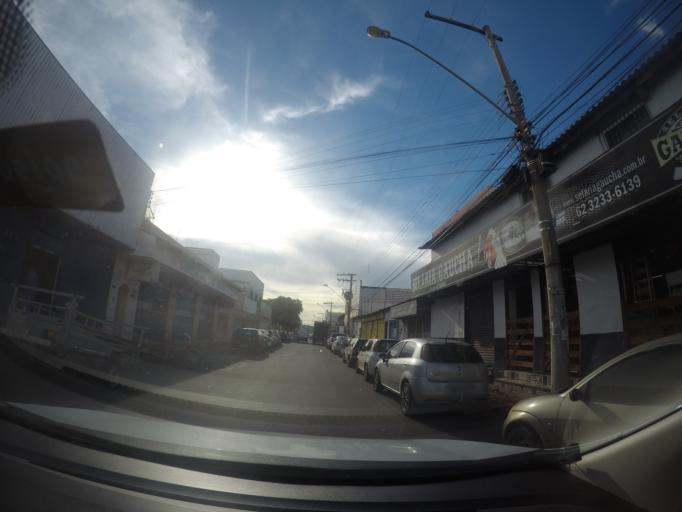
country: BR
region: Goias
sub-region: Goiania
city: Goiania
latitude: -16.6723
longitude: -49.2934
